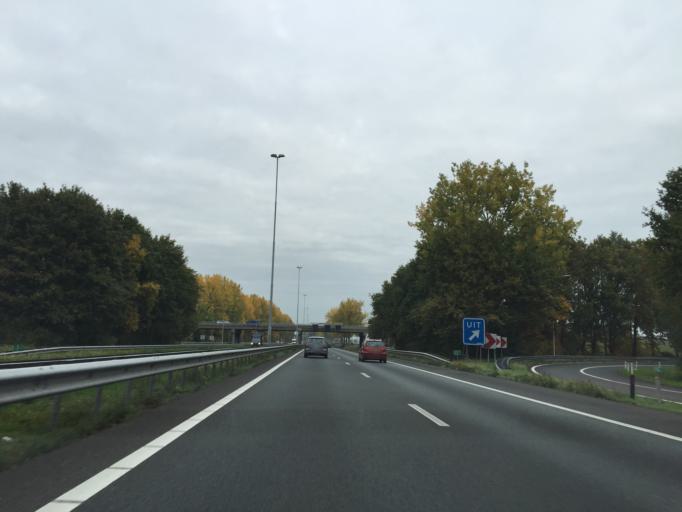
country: NL
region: North Brabant
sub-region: Gemeente Oosterhout
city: Oosterhout
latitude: 51.6480
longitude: 4.8826
